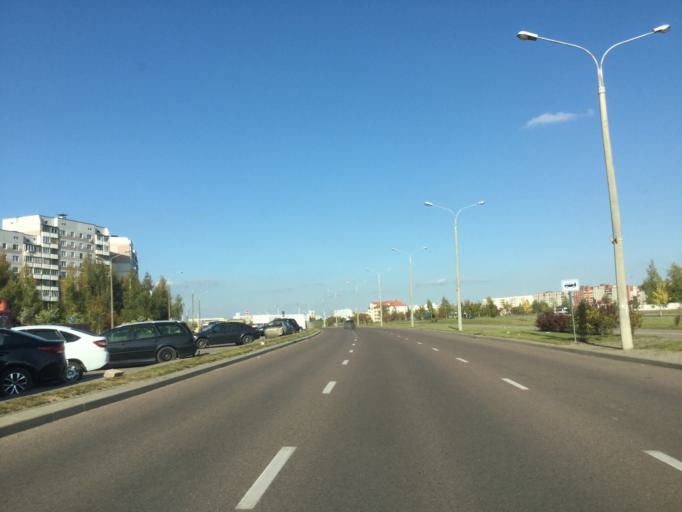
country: BY
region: Vitebsk
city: Vitebsk
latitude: 55.1592
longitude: 30.2193
